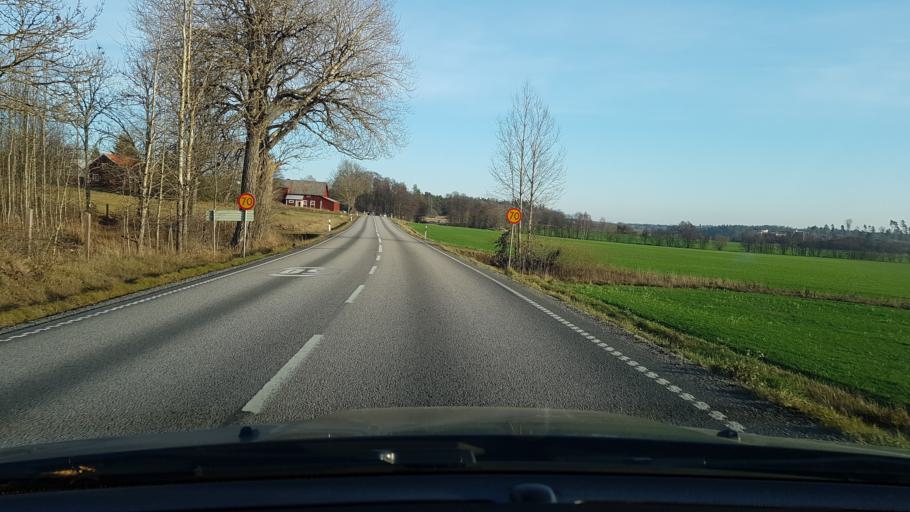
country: SE
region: Stockholm
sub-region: Norrtalje Kommun
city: Nykvarn
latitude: 59.7392
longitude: 18.1626
